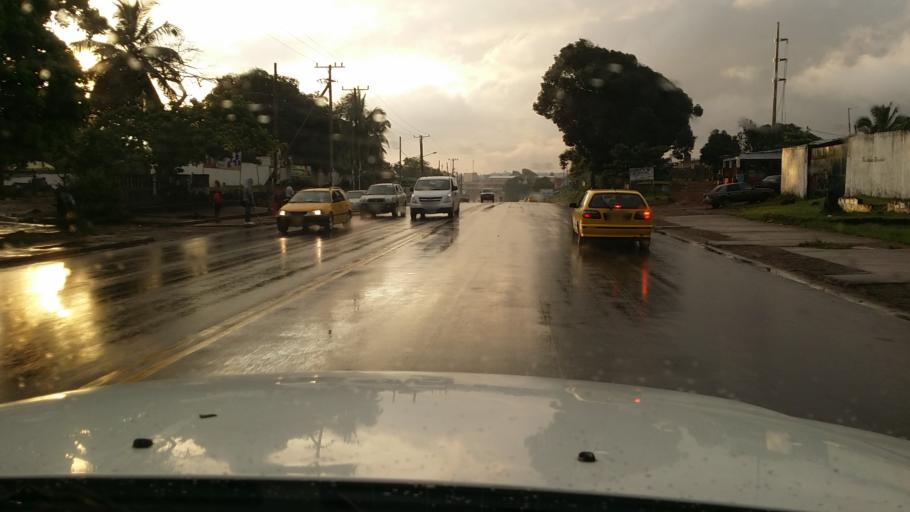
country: LR
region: Montserrado
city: Monrovia
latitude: 6.2658
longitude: -10.7202
